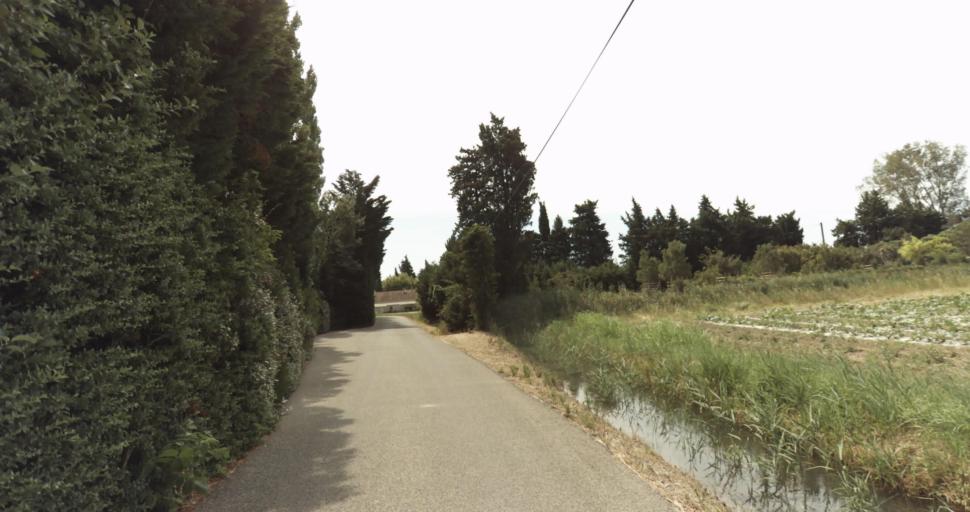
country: FR
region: Provence-Alpes-Cote d'Azur
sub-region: Departement du Vaucluse
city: Althen-des-Paluds
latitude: 44.0342
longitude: 4.9599
